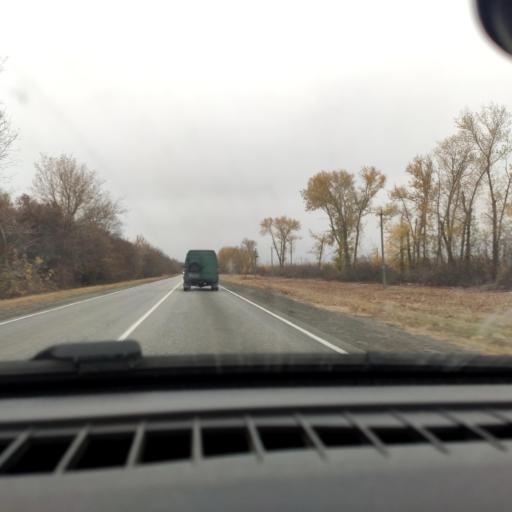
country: RU
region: Voronezj
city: Uryv-Pokrovka
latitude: 51.0830
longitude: 39.0010
